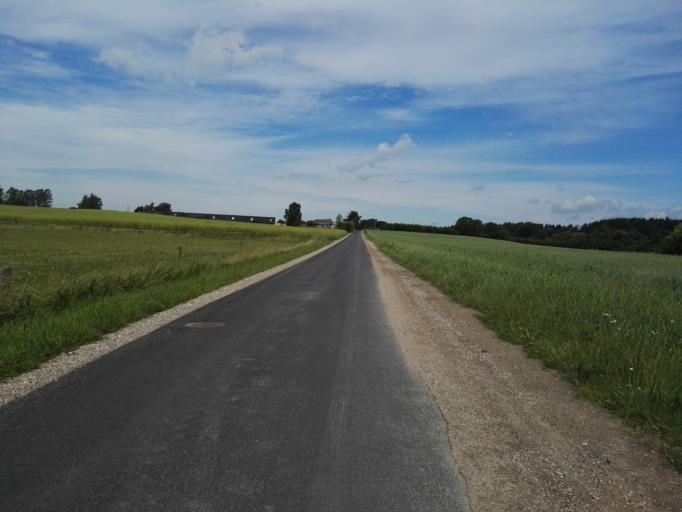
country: DK
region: Capital Region
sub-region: Egedal Kommune
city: Olstykke
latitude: 55.8114
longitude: 12.1786
